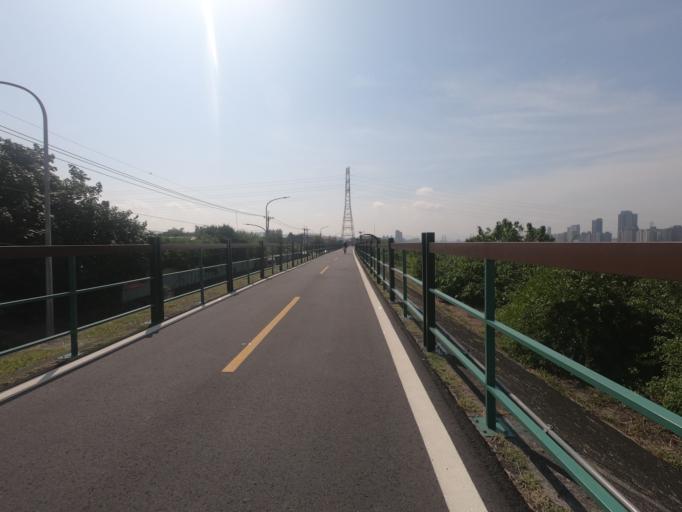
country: TW
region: Taipei
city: Taipei
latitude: 25.1010
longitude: 121.4870
